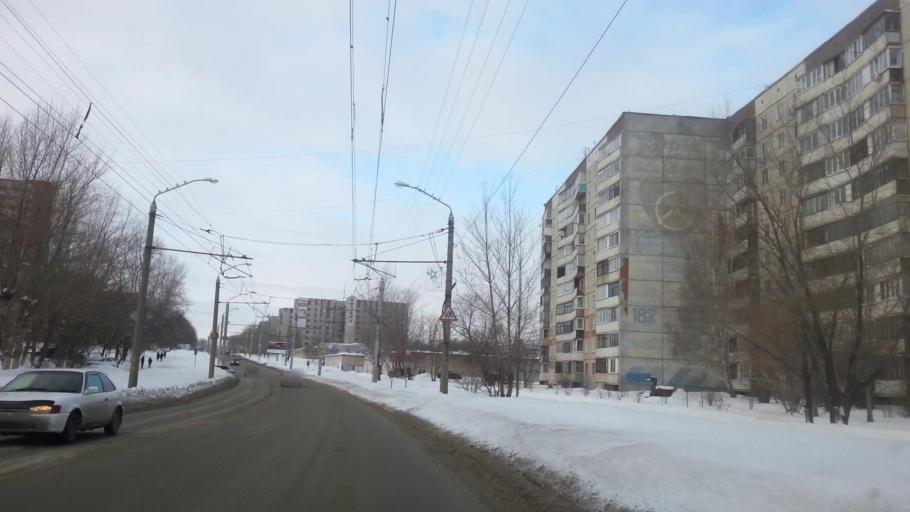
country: RU
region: Altai Krai
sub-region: Gorod Barnaulskiy
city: Barnaul
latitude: 53.3688
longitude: 83.7036
